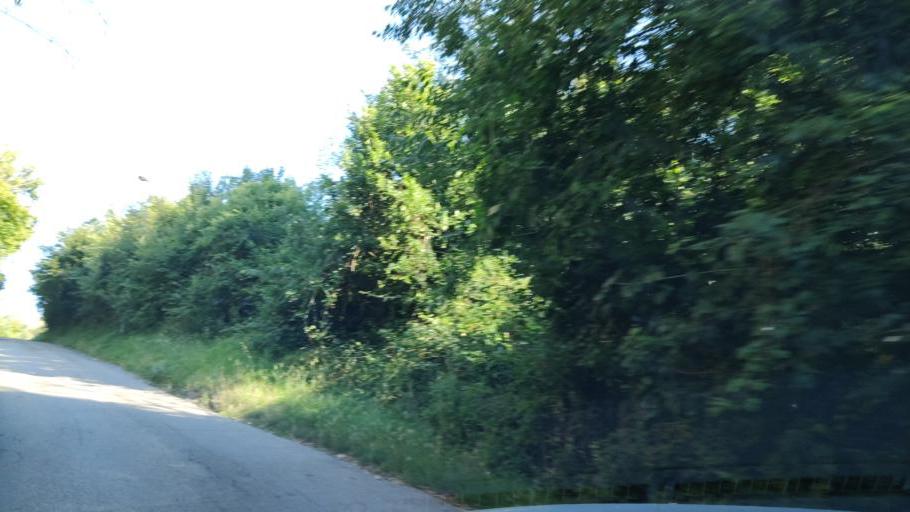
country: IT
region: Umbria
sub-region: Provincia di Terni
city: Narni
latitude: 42.5204
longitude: 12.5194
